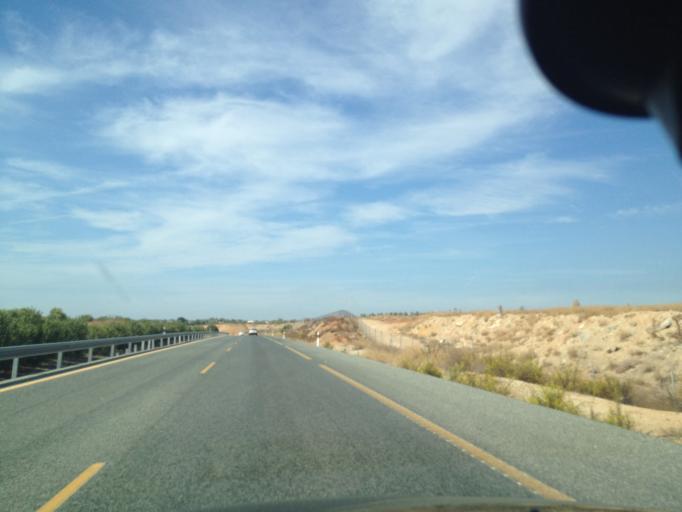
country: ES
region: Andalusia
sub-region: Provincia de Sevilla
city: La Puebla de Cazalla
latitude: 37.2340
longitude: -5.3096
